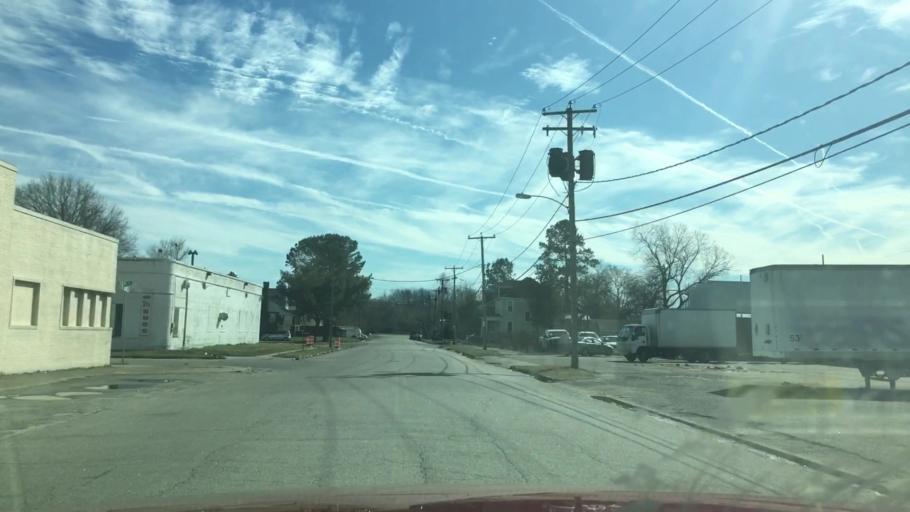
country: US
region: Virginia
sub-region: City of Portsmouth
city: Portsmouth
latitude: 36.8343
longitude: -76.3292
